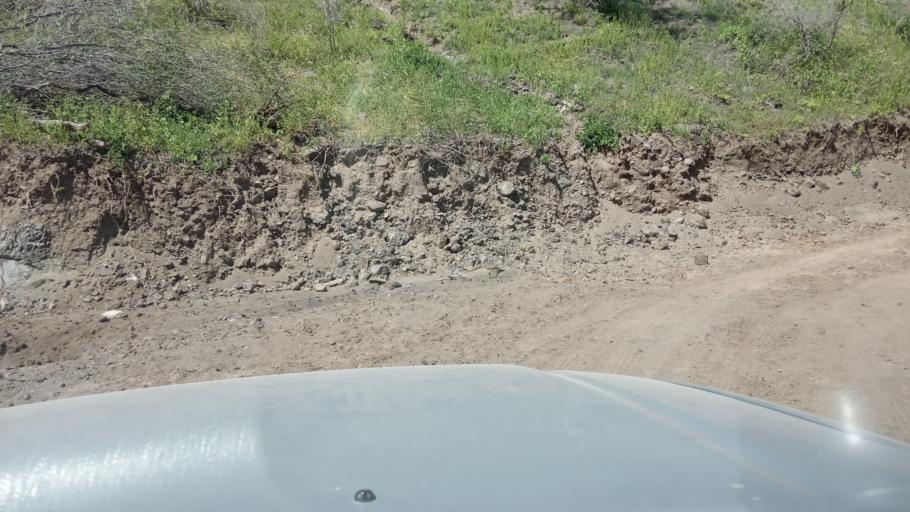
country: CV
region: Santa Catarina
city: Assomada
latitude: 15.1129
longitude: -23.7289
